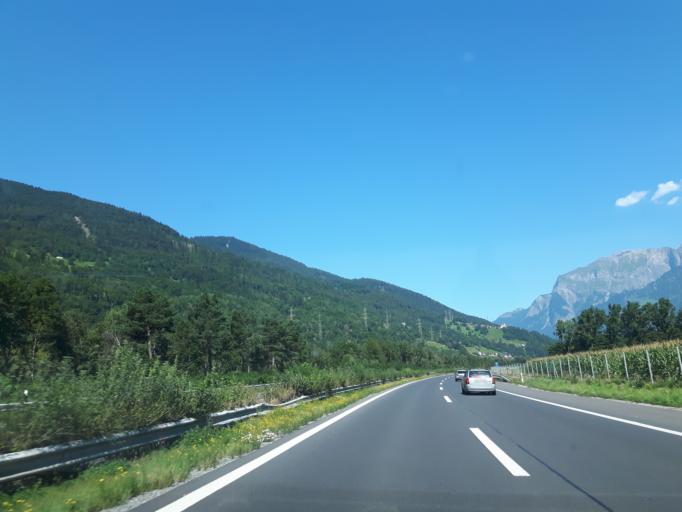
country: CH
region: Grisons
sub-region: Landquart District
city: Untervaz
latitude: 46.9431
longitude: 9.5463
